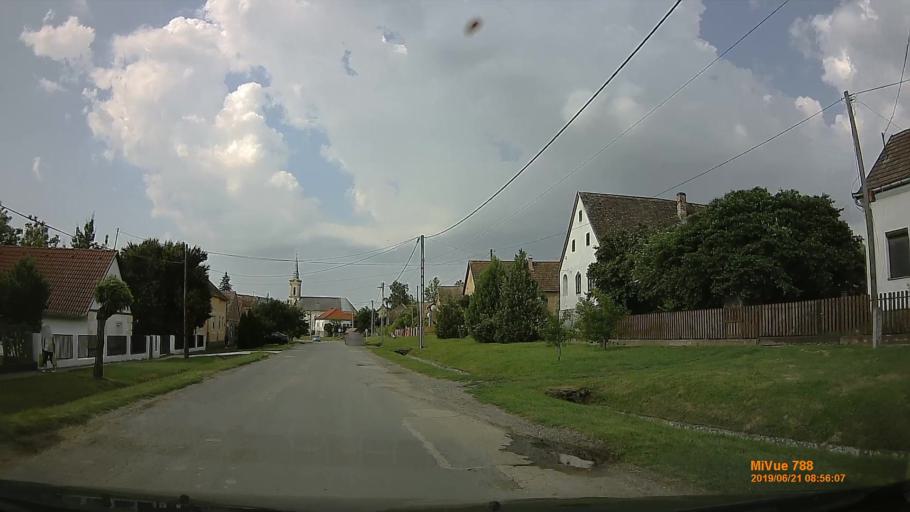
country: HU
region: Baranya
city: Buekkoesd
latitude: 46.1588
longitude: 17.8754
